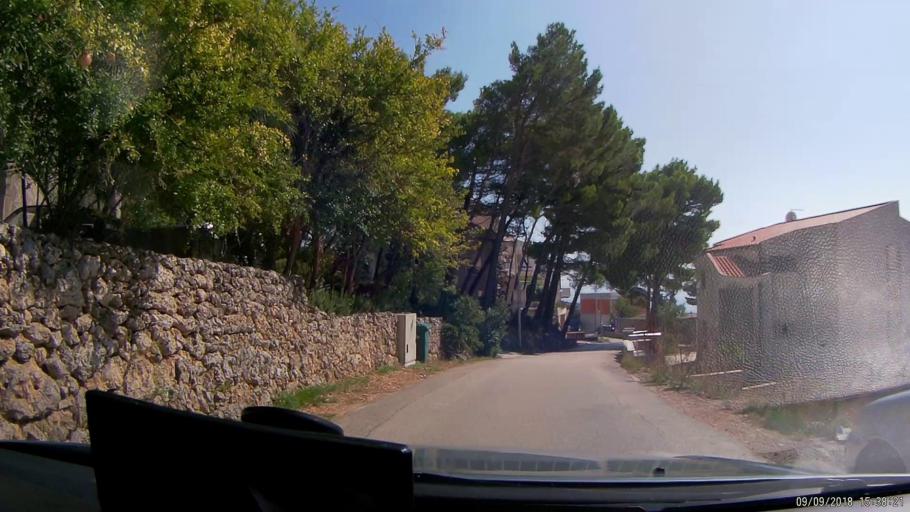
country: HR
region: Splitsko-Dalmatinska
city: Donja Brela
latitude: 43.3705
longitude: 16.9312
